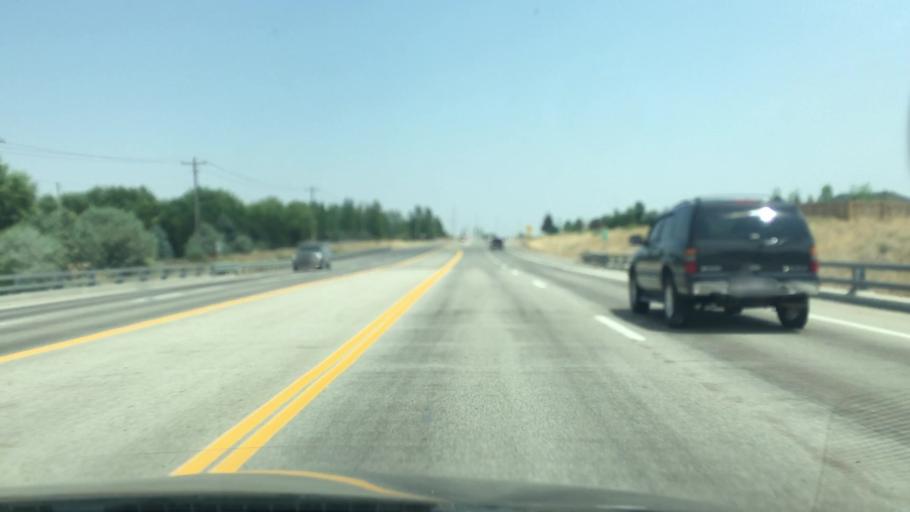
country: US
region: Idaho
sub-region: Twin Falls County
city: Twin Falls
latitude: 42.5934
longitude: -114.5291
